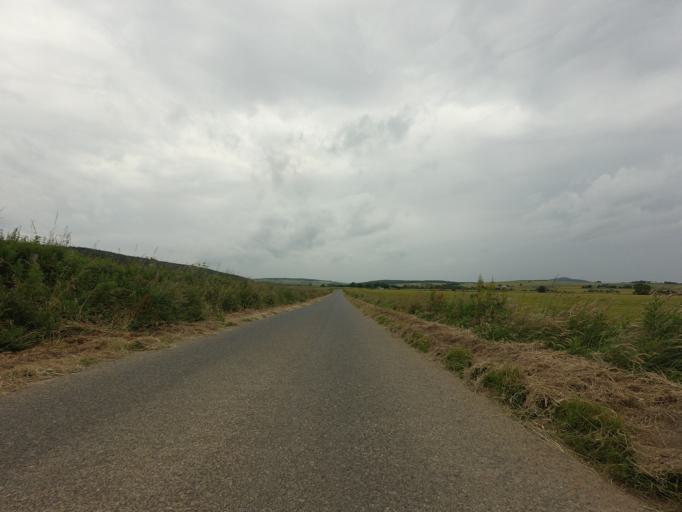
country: GB
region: Scotland
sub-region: Aberdeenshire
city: Portsoy
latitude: 57.6647
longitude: -2.7321
